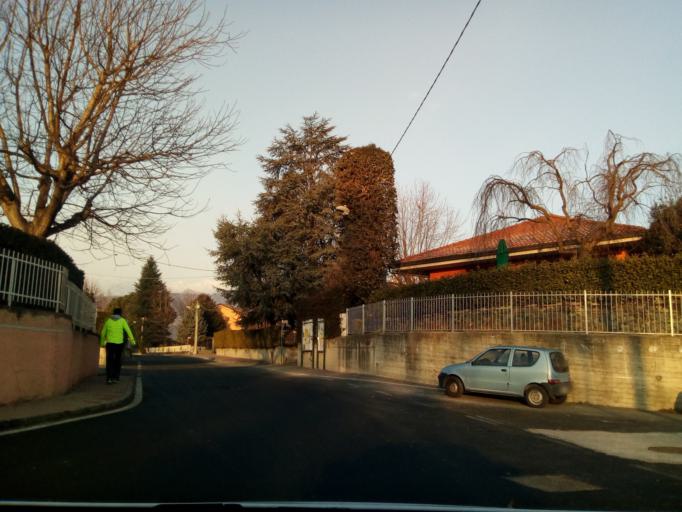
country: IT
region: Piedmont
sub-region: Provincia di Torino
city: Salerano Canavese
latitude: 45.4604
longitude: 7.8504
